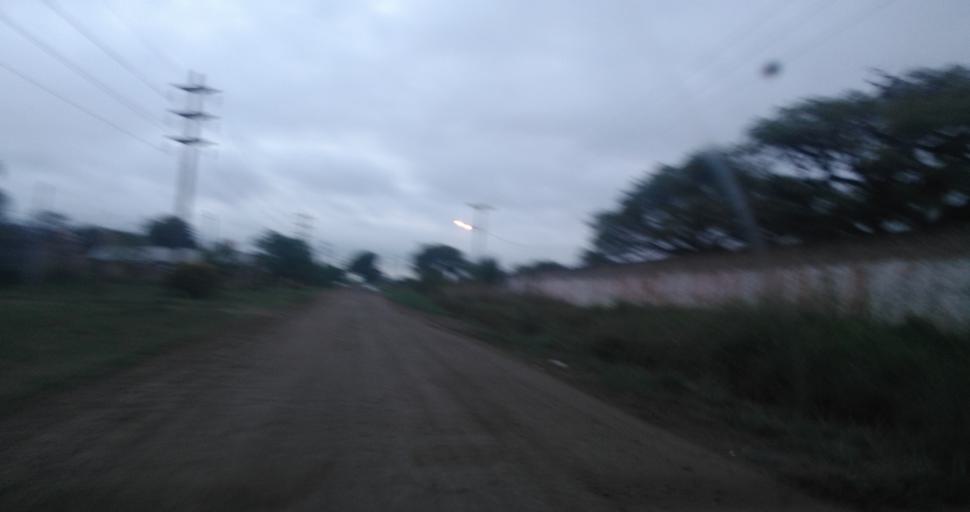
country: AR
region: Chaco
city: Fontana
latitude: -27.3984
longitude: -59.0010
